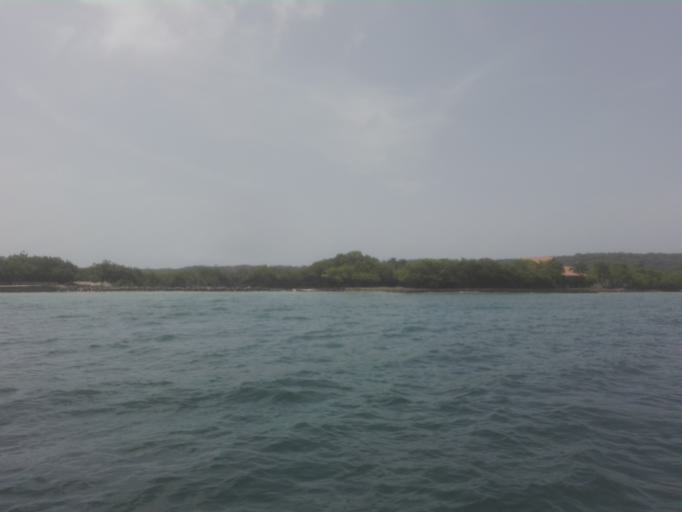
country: CO
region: Bolivar
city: Turbana
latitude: 10.1684
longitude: -75.6694
